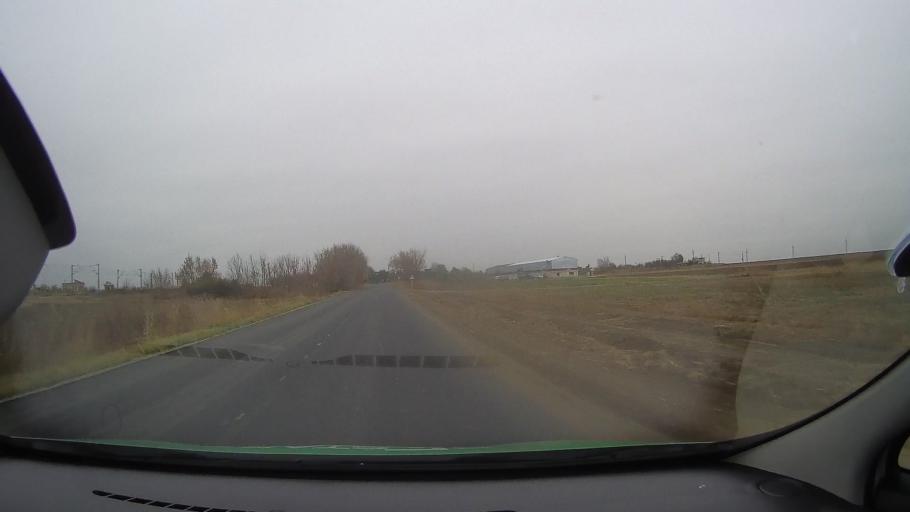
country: RO
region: Ialomita
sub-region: Comuna Valea Ciorii
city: Valea Ciorii
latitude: 44.7387
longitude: 27.5777
